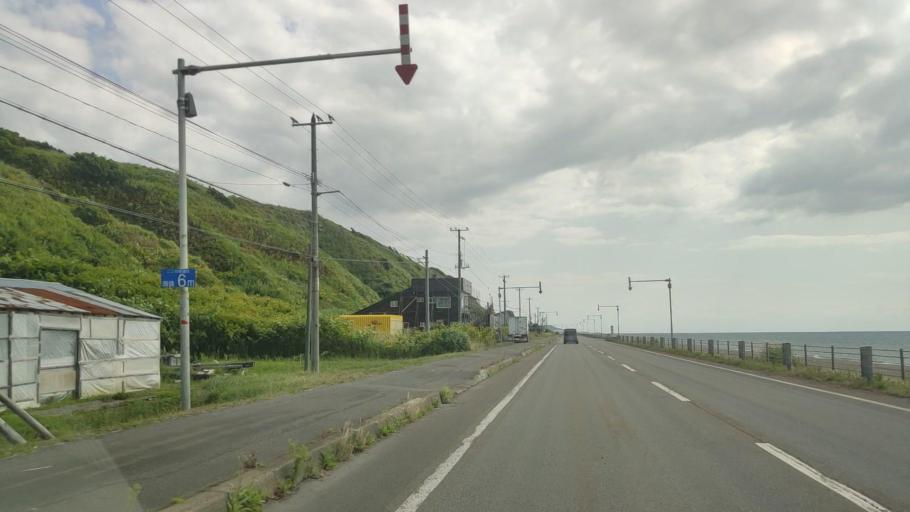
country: JP
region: Hokkaido
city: Rumoi
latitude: 44.2000
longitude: 141.6579
